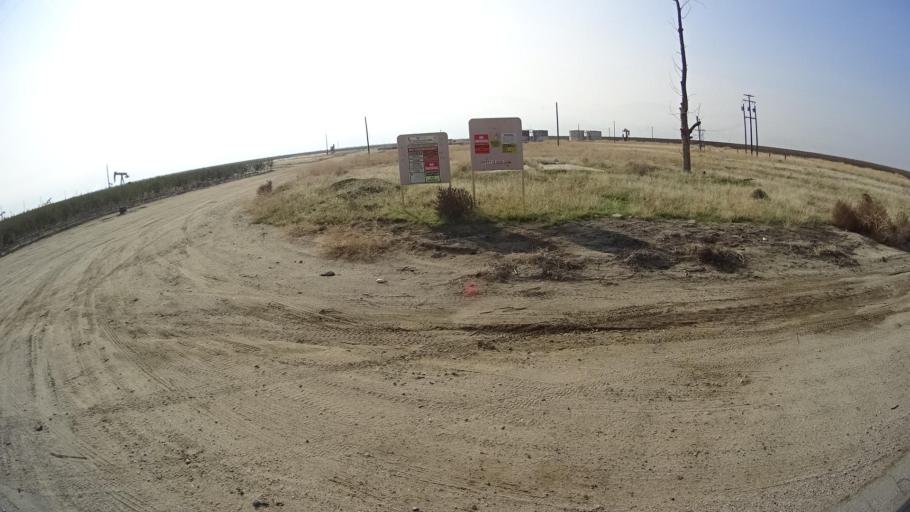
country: US
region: California
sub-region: Kern County
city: Lebec
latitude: 34.9930
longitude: -118.8910
